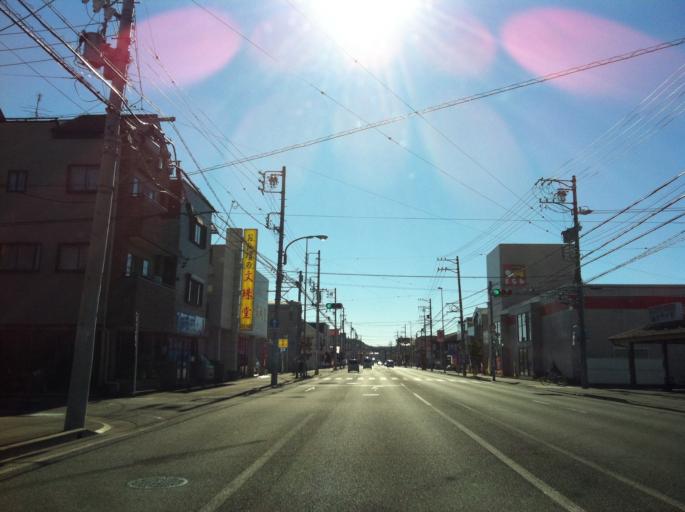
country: JP
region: Shizuoka
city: Shizuoka-shi
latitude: 35.0035
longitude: 138.3903
